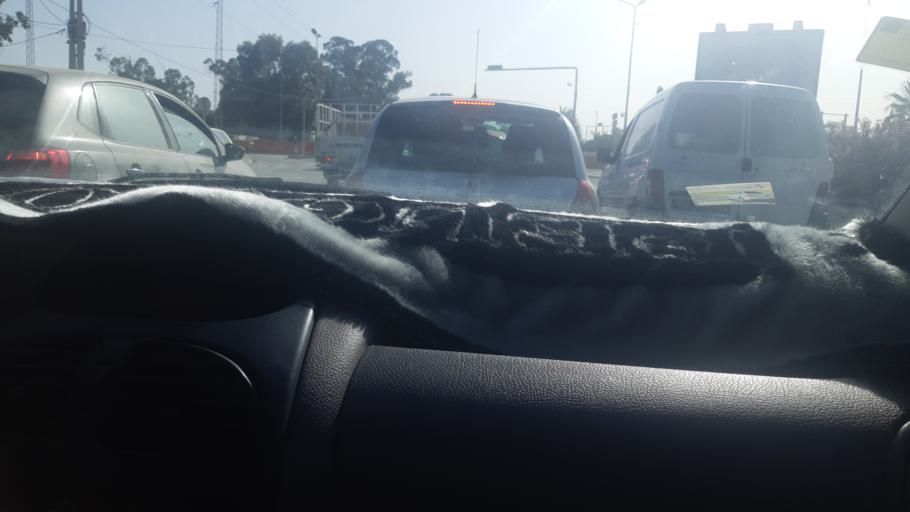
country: TN
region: Safaqis
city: Sfax
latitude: 34.7336
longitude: 10.7252
